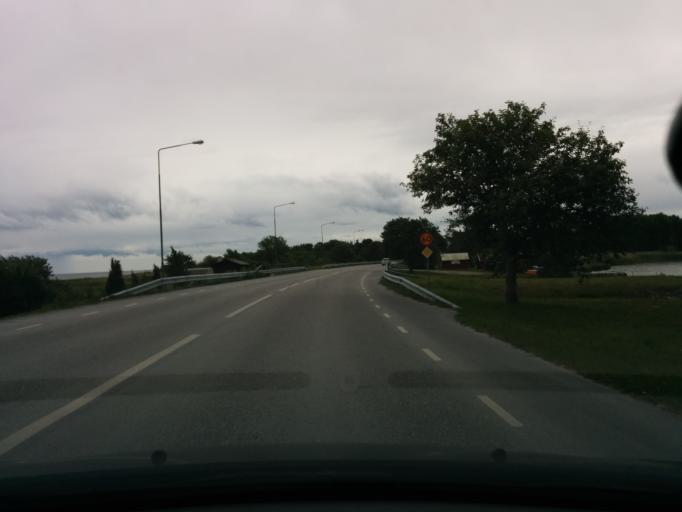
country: SE
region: Gotland
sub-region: Gotland
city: Slite
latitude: 57.6956
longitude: 18.7985
